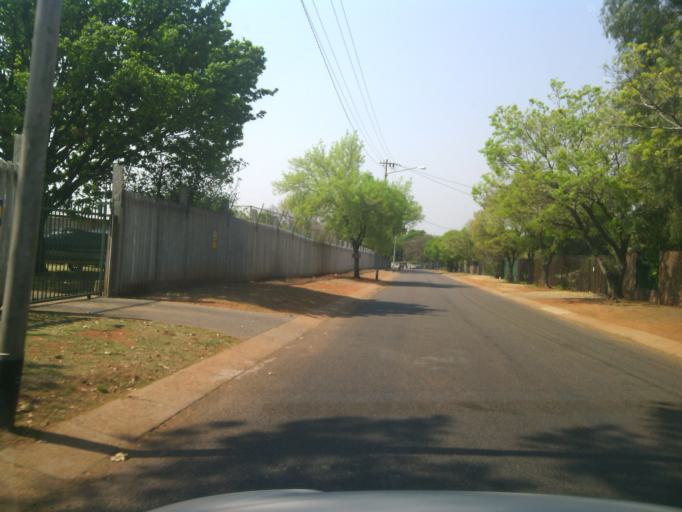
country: ZA
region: Gauteng
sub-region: City of Tshwane Metropolitan Municipality
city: Centurion
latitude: -25.8362
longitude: 28.2000
